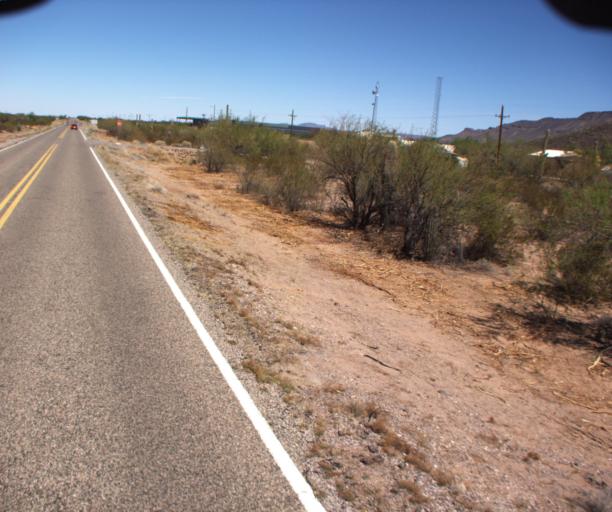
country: US
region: Arizona
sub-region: Pima County
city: Ajo
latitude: 32.2716
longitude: -112.7402
